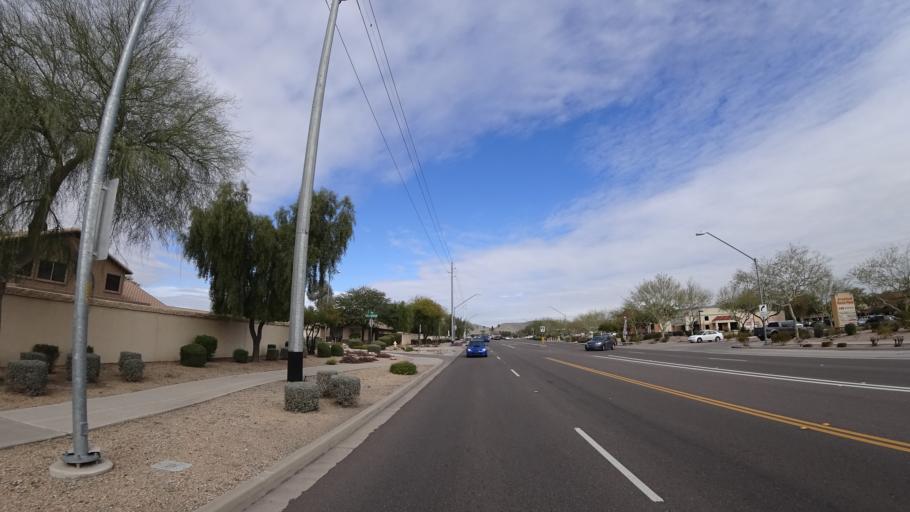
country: US
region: Arizona
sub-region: Maricopa County
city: Peoria
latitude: 33.6526
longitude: -112.1864
